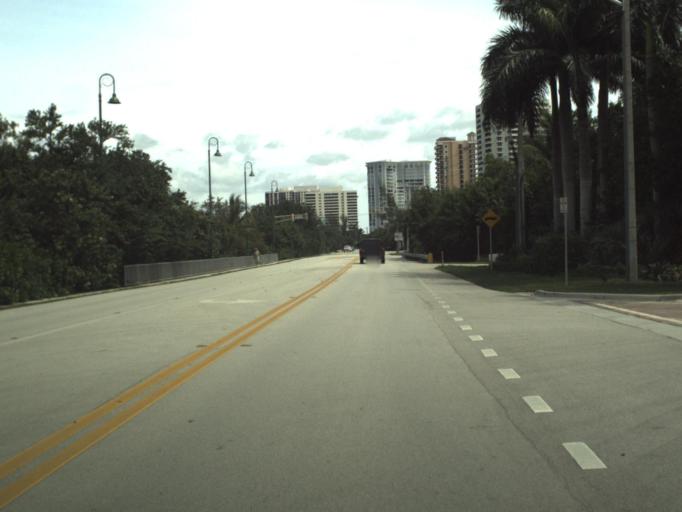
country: US
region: Florida
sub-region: Palm Beach County
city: Palm Beach Shores
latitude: 26.7976
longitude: -80.0343
